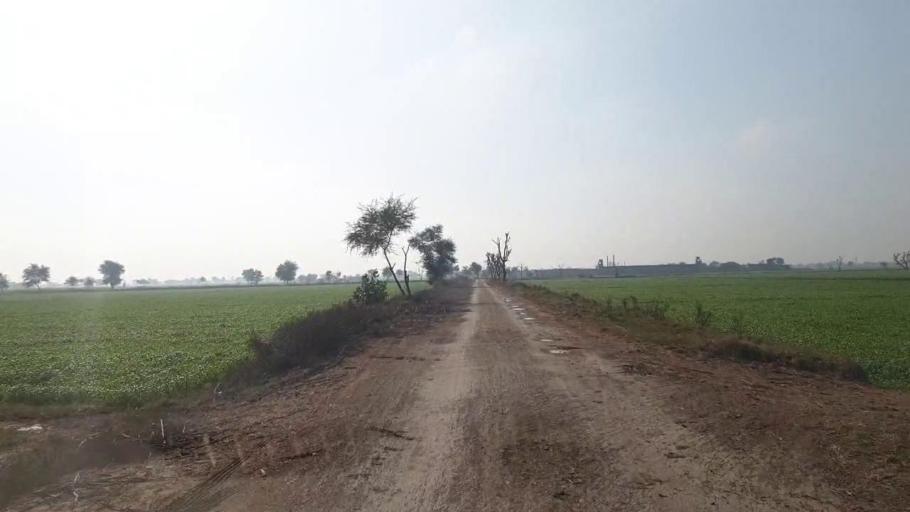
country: PK
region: Sindh
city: Shahdadpur
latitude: 25.9955
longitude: 68.6246
